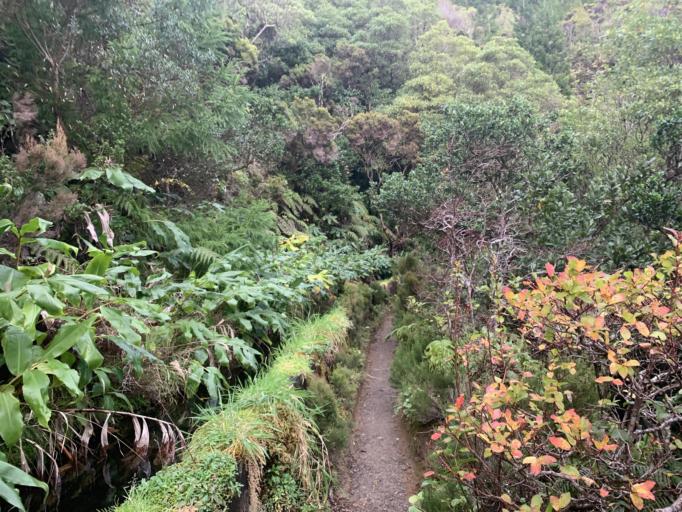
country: PT
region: Azores
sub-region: Vila Franca do Campo
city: Vila Franca do Campo
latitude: 37.7474
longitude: -25.4756
